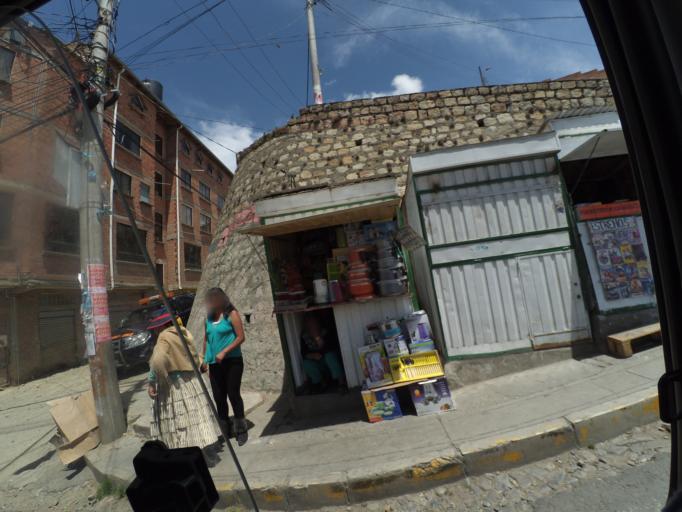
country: BO
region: La Paz
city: La Paz
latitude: -16.4943
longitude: -68.1273
